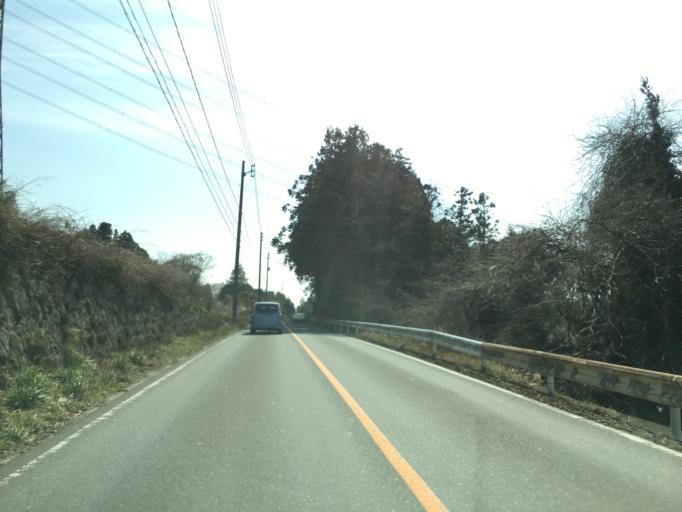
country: JP
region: Ibaraki
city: Daigo
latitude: 36.9327
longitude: 140.4152
